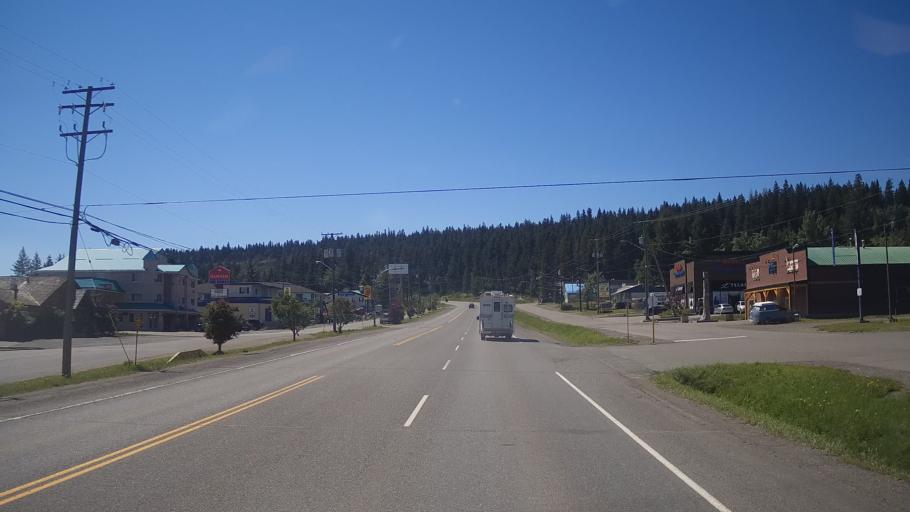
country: CA
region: British Columbia
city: Cache Creek
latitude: 51.6319
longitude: -121.3003
